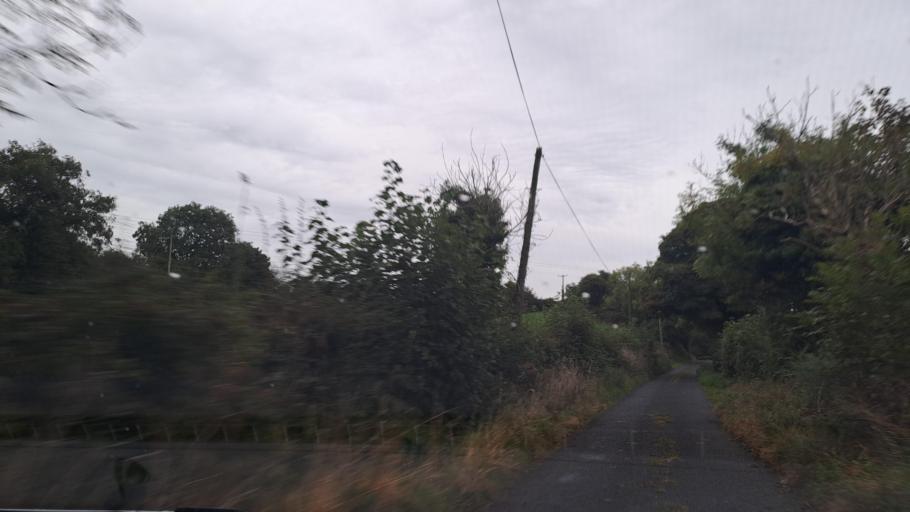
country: IE
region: Ulster
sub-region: County Monaghan
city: Carrickmacross
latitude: 53.9862
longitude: -6.7929
